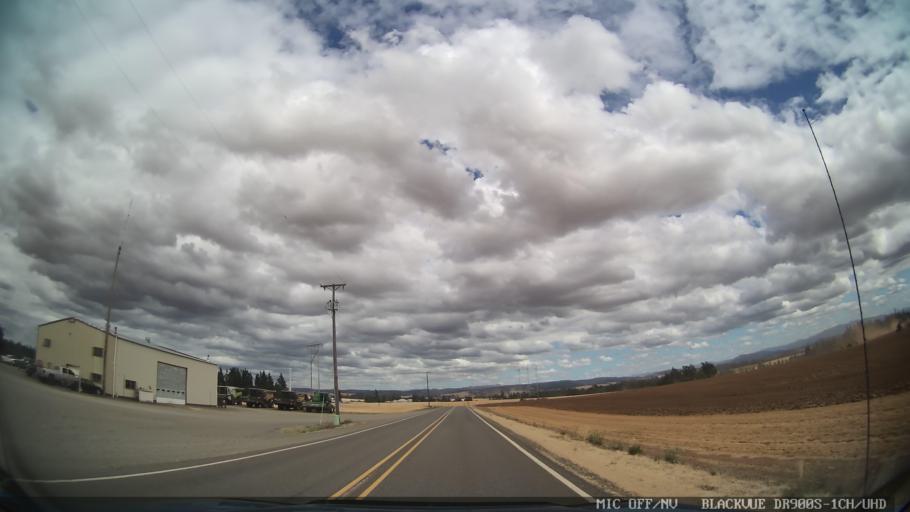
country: US
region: Oregon
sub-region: Marion County
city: Sublimity
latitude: 44.8654
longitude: -122.8147
